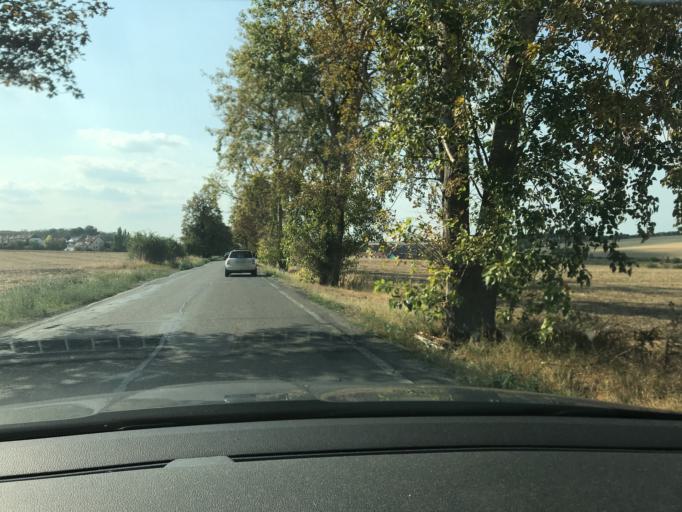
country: CZ
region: Central Bohemia
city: Velke Prilepy
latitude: 50.1556
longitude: 14.3264
